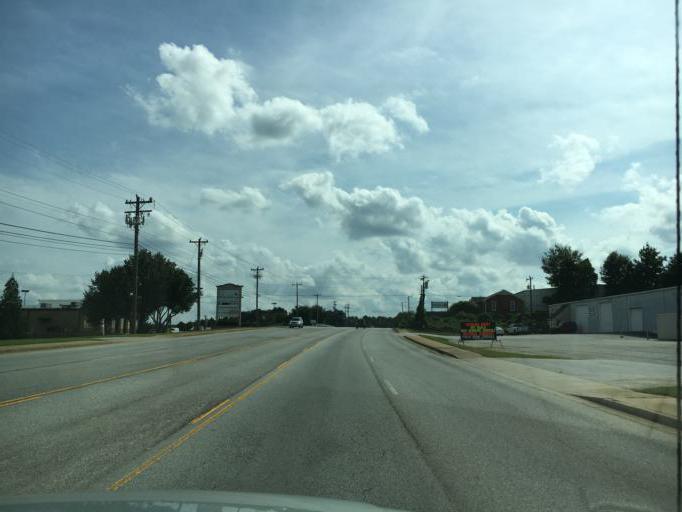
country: US
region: South Carolina
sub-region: Greenville County
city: Five Forks
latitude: 34.8537
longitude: -82.2280
